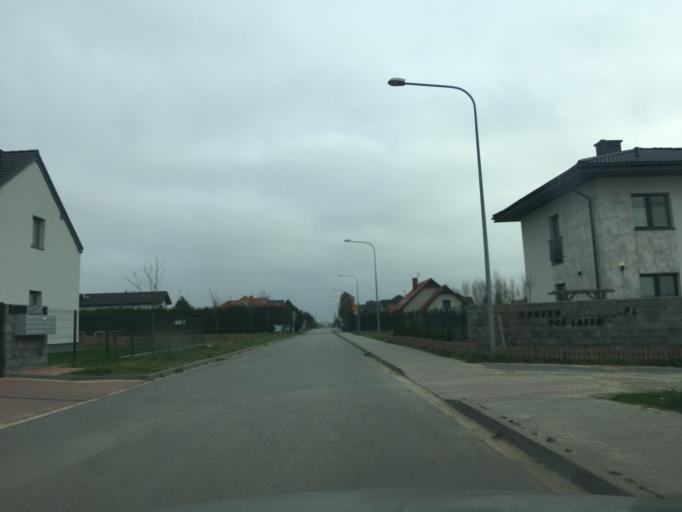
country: PL
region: Masovian Voivodeship
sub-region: Powiat piaseczynski
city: Lesznowola
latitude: 52.0844
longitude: 20.9440
